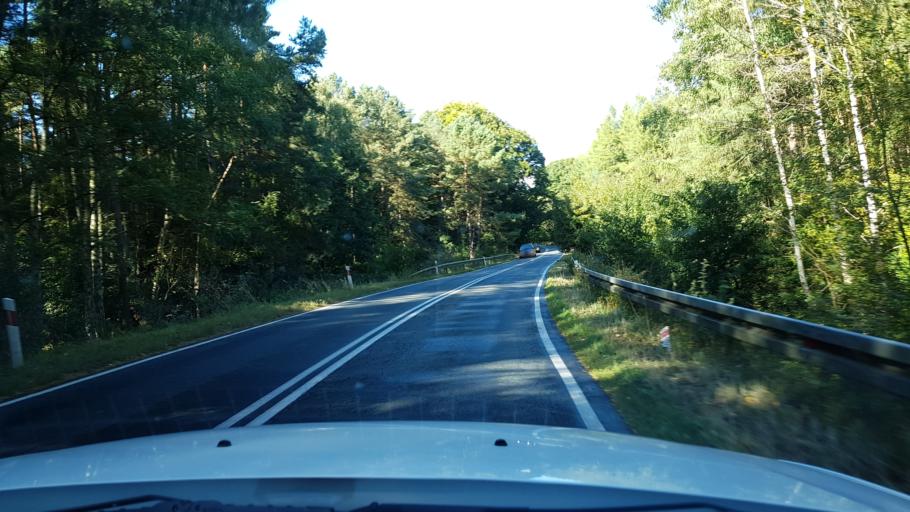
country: PL
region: West Pomeranian Voivodeship
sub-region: Powiat gryfinski
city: Gryfino
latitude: 53.1928
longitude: 14.5255
